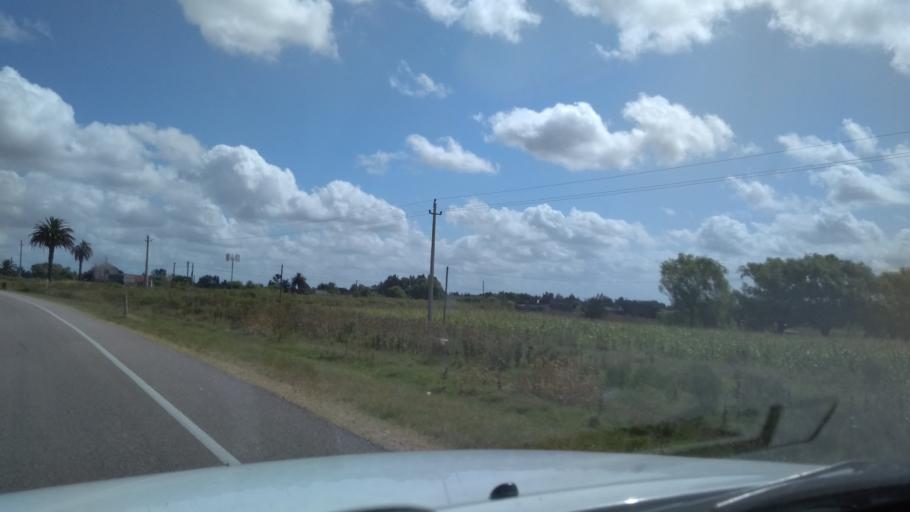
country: UY
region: Canelones
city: Sauce
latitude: -34.6554
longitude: -56.0543
